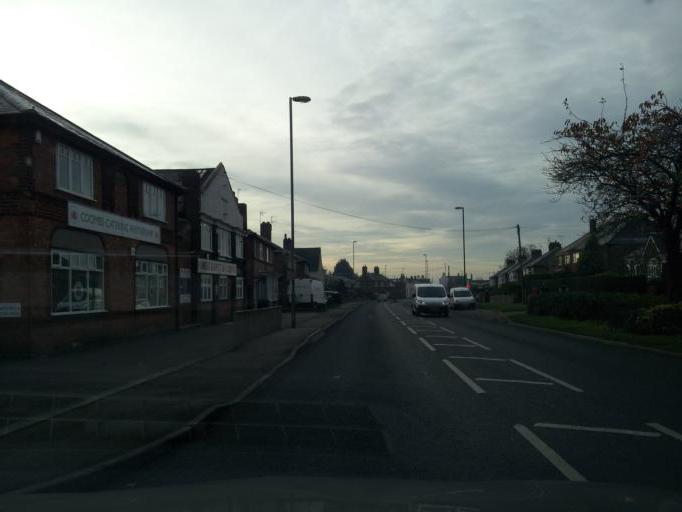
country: GB
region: England
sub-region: Leicestershire
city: Lutterworth
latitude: 52.4596
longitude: -1.1987
